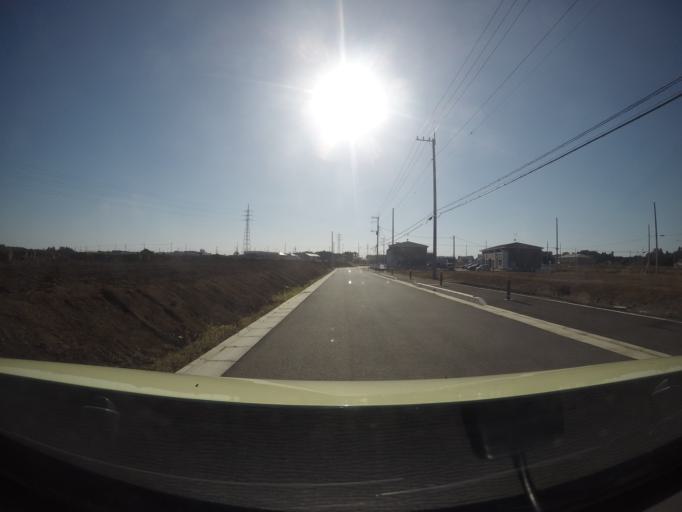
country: JP
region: Ibaraki
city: Naka
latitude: 36.1063
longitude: 140.1245
